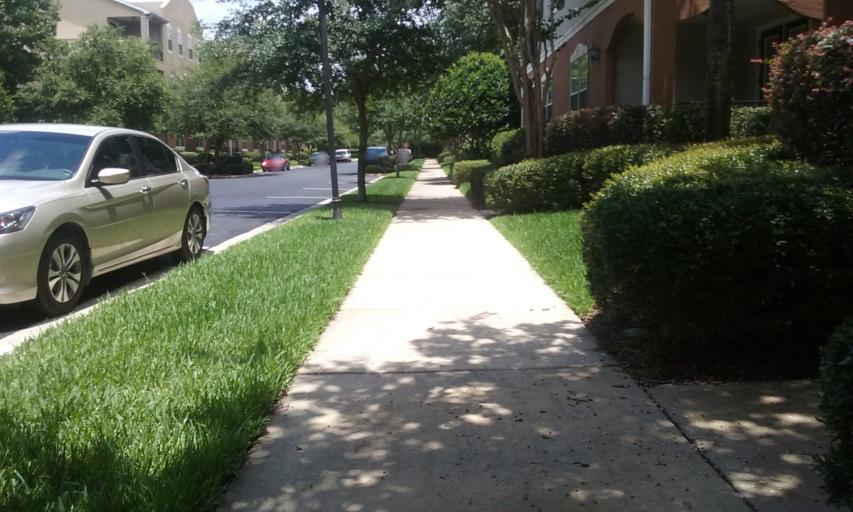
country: US
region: Florida
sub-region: Alachua County
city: Gainesville
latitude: 29.6854
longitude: -82.3579
